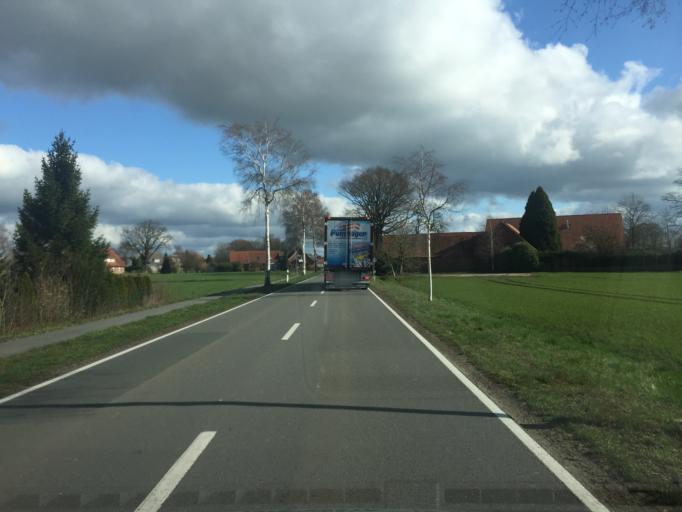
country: DE
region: Lower Saxony
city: Affinghausen
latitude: 52.7788
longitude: 8.8735
